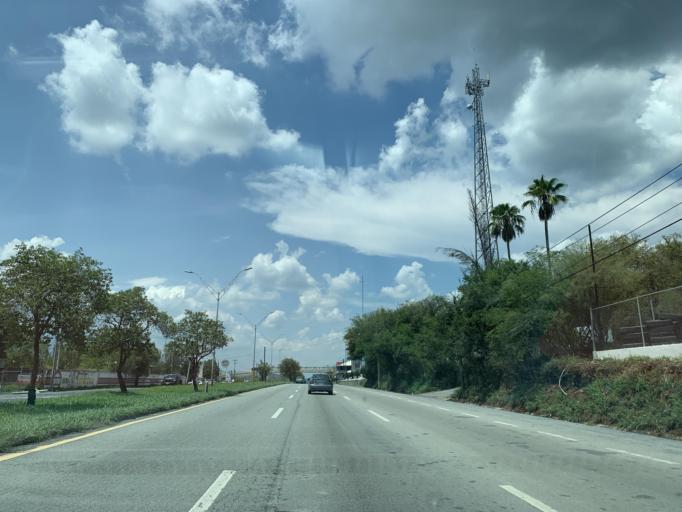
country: MX
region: Nuevo Leon
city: Santiago
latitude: 25.3882
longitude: -100.1175
